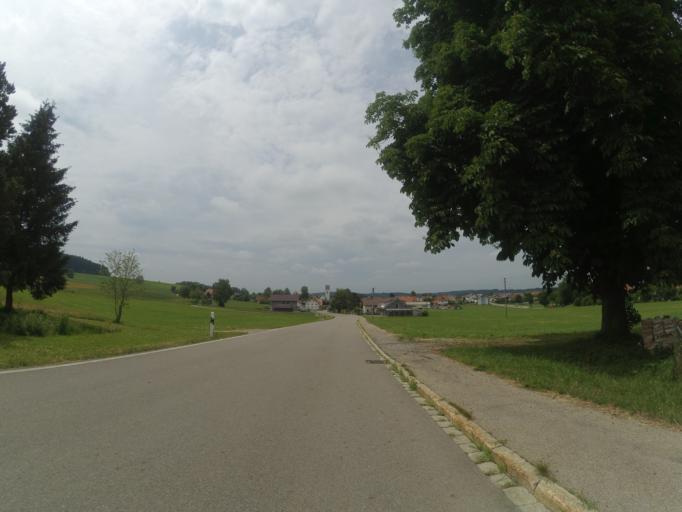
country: DE
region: Baden-Wuerttemberg
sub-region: Tuebingen Region
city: Isny im Allgau
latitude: 47.7418
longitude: 10.0170
